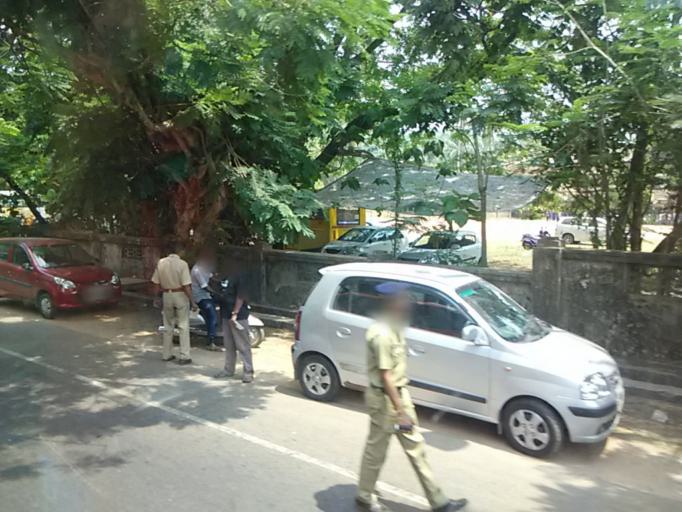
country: IN
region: Kerala
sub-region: Kozhikode
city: Kozhikode
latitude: 11.2869
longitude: 75.7677
